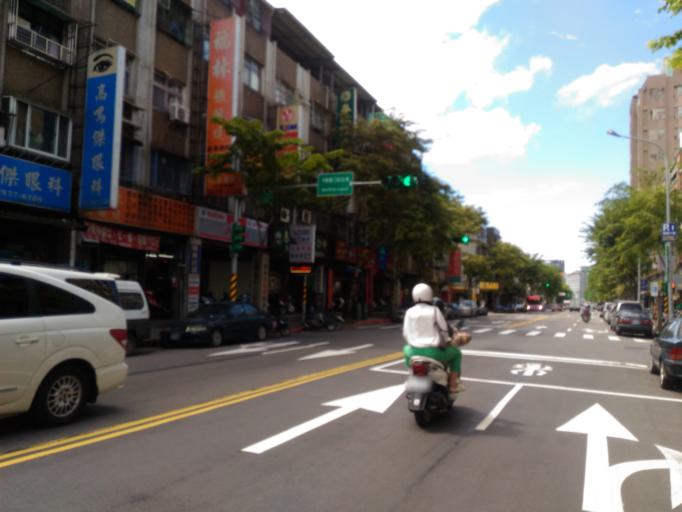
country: TW
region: Taipei
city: Taipei
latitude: 24.9815
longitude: 121.5594
